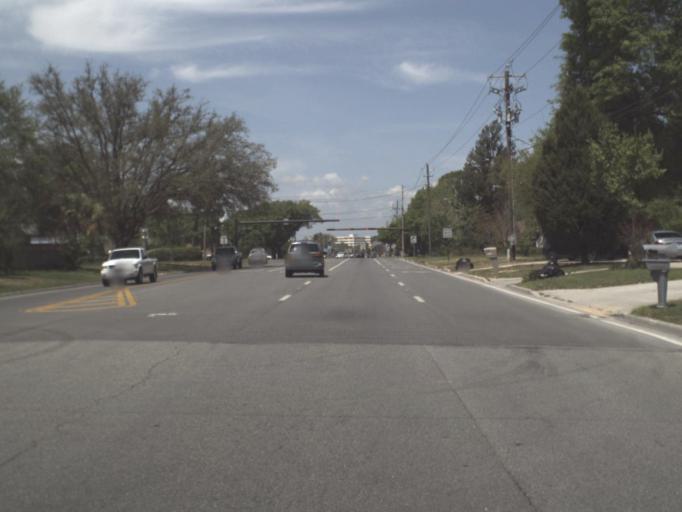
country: US
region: Florida
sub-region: Escambia County
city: Goulding
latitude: 30.4642
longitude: -87.2031
